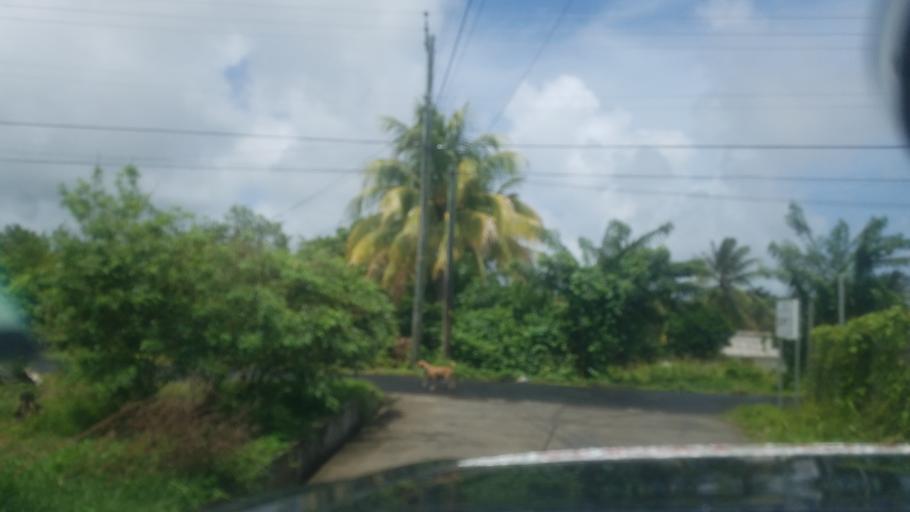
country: LC
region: Laborie Quarter
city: Laborie
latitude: 13.7574
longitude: -60.9760
